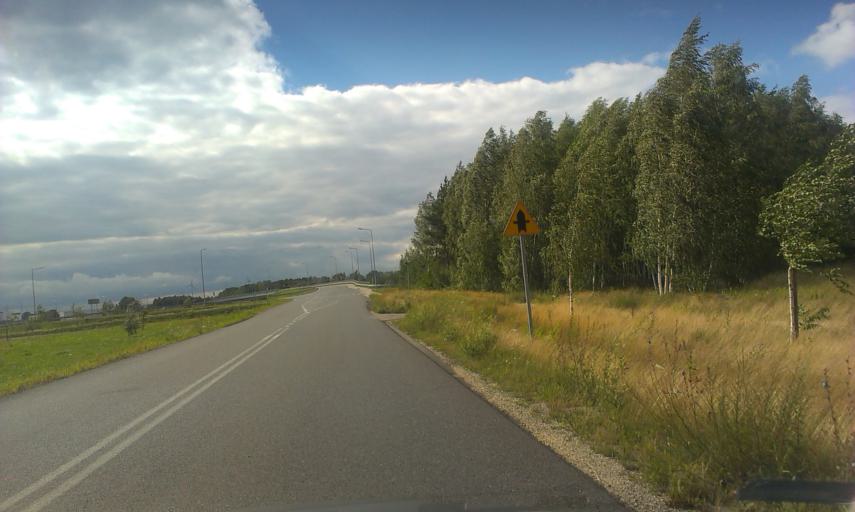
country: PL
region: Masovian Voivodeship
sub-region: Powiat zyrardowski
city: Radziejowice
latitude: 51.9707
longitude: 20.5763
